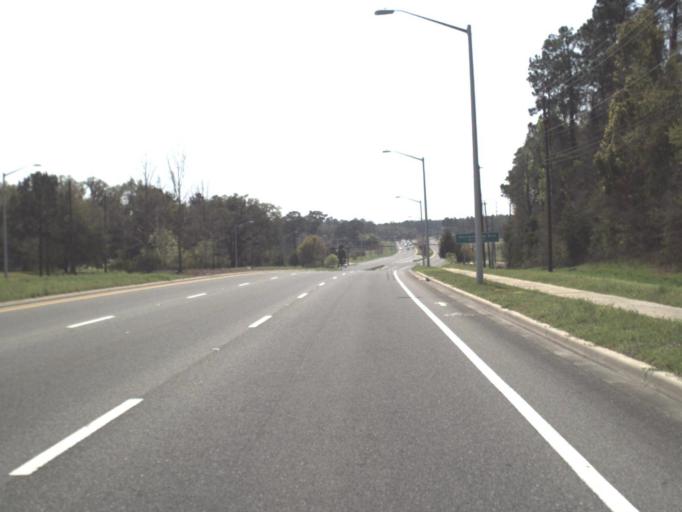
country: US
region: Florida
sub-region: Leon County
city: Tallahassee
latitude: 30.3957
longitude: -84.2352
